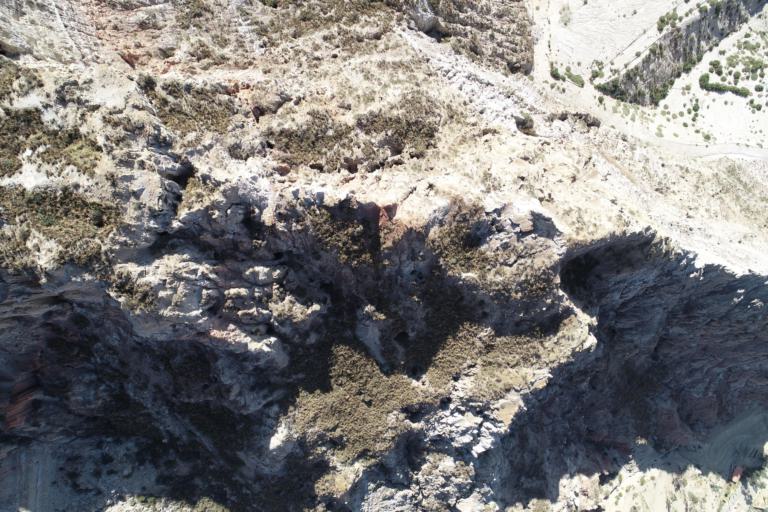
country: BO
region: La Paz
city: La Paz
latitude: -16.5538
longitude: -68.1096
